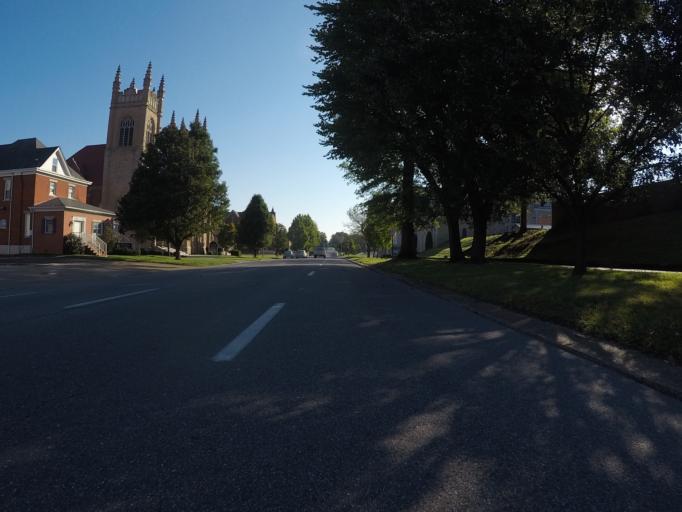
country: US
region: West Virginia
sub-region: Cabell County
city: Huntington
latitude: 38.4200
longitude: -82.4398
